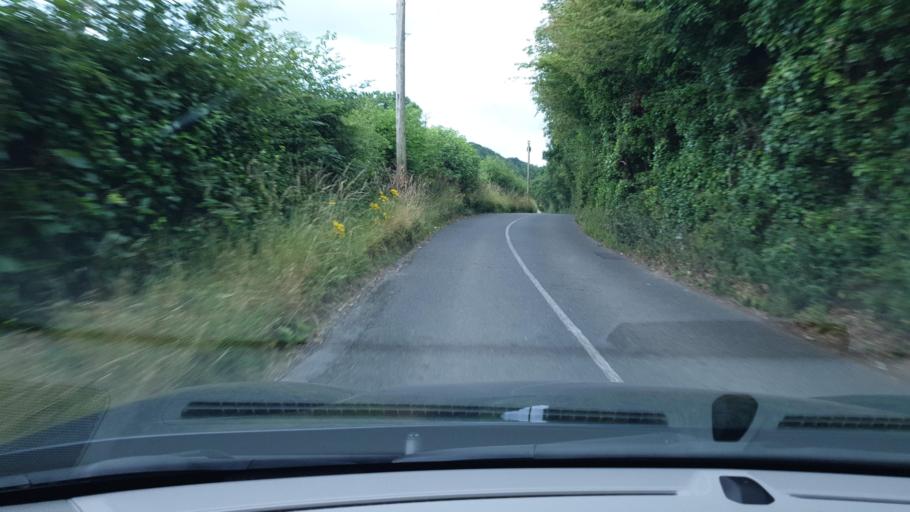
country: IE
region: Leinster
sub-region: South Dublin
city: Saggart
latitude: 53.2678
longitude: -6.4476
